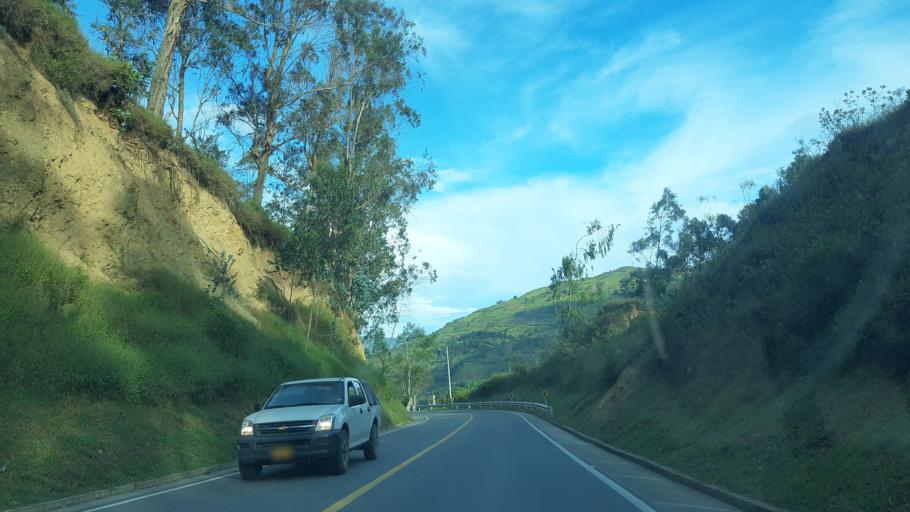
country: CO
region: Cundinamarca
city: Macheta
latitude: 5.0773
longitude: -73.5998
